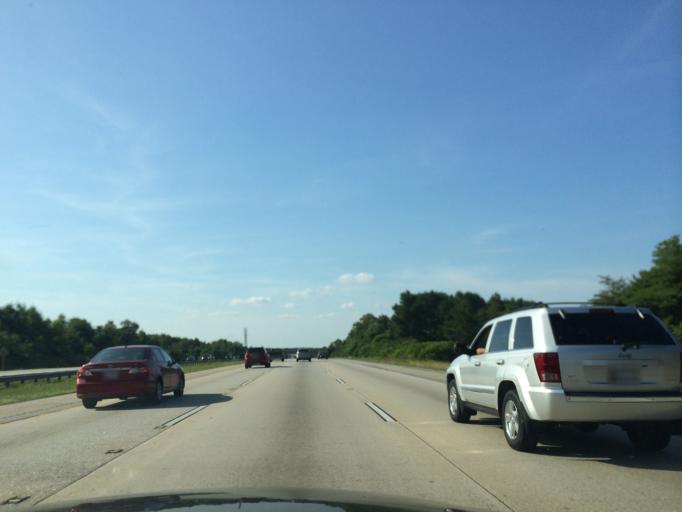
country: US
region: Maryland
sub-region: Anne Arundel County
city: South Gate
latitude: 39.0905
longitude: -76.6253
